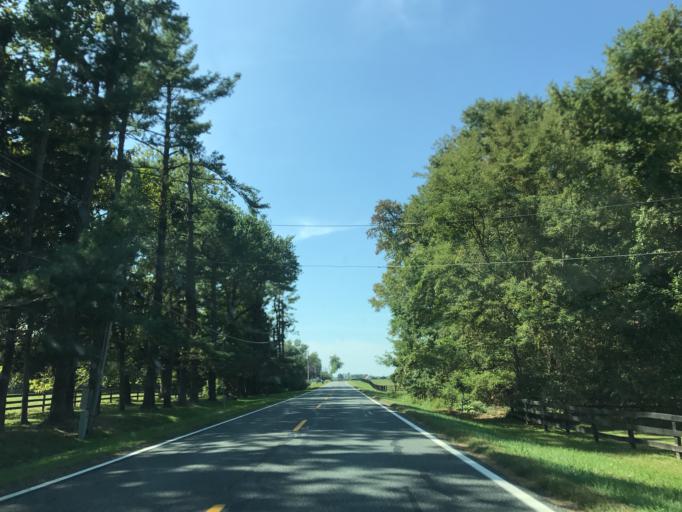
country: US
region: Maryland
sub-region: Cecil County
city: Elkton
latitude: 39.4905
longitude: -75.8308
